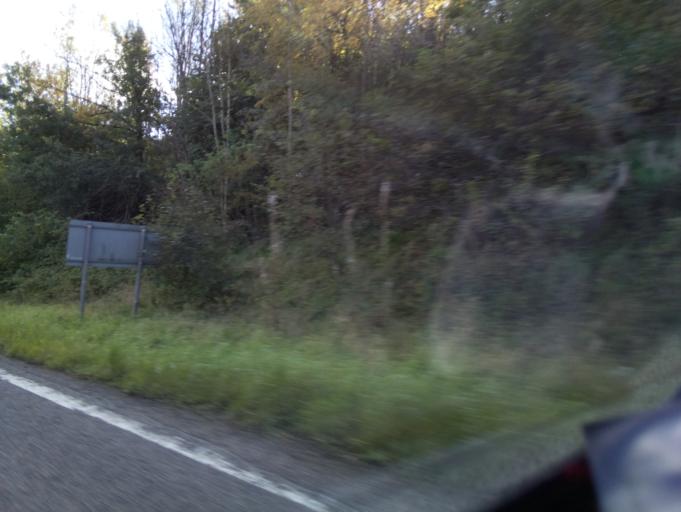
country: GB
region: Wales
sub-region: Merthyr Tydfil County Borough
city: Merthyr Tydfil
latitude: 51.7607
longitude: -3.4120
